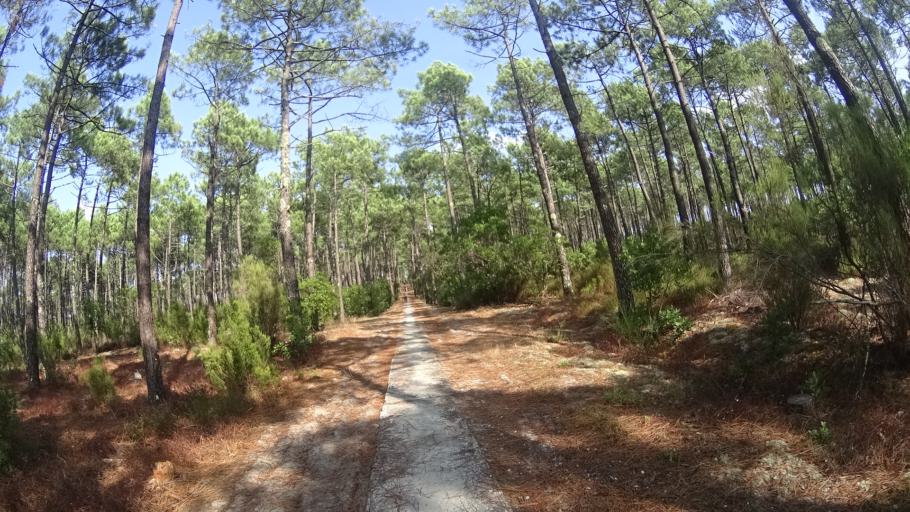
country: FR
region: Aquitaine
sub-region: Departement de la Gironde
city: Lacanau
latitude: 44.9633
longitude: -1.1988
